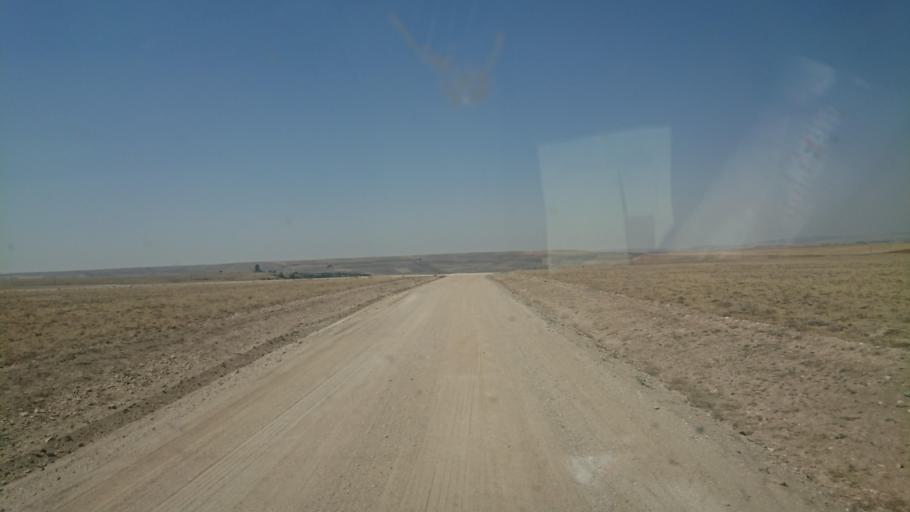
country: TR
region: Aksaray
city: Agacoren
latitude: 38.7386
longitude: 33.8763
